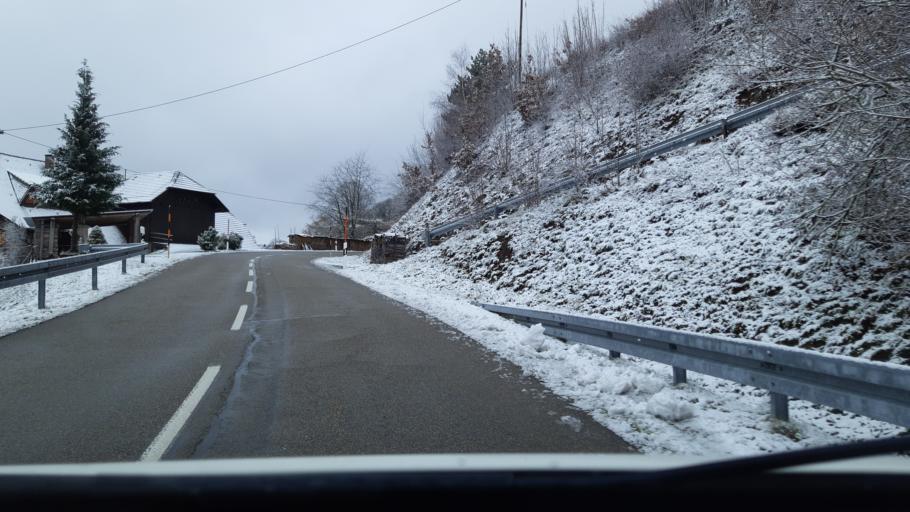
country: DE
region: Baden-Wuerttemberg
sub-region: Freiburg Region
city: Horben
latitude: 47.9181
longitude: 7.8482
